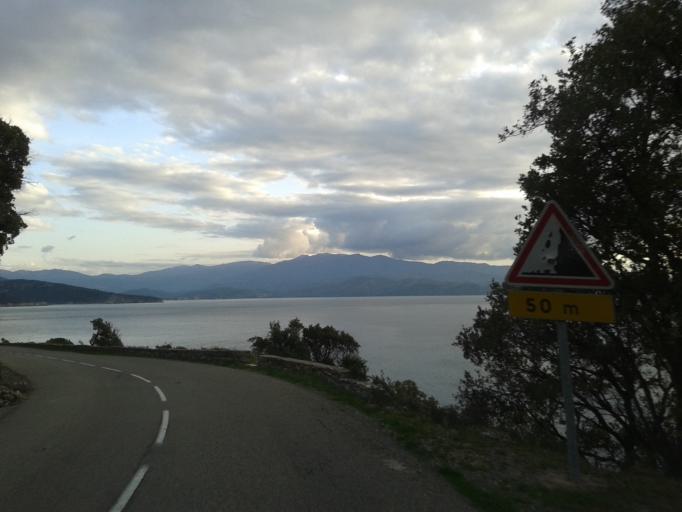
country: FR
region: Corsica
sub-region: Departement de la Haute-Corse
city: Saint-Florent
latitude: 42.7646
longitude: 9.3379
